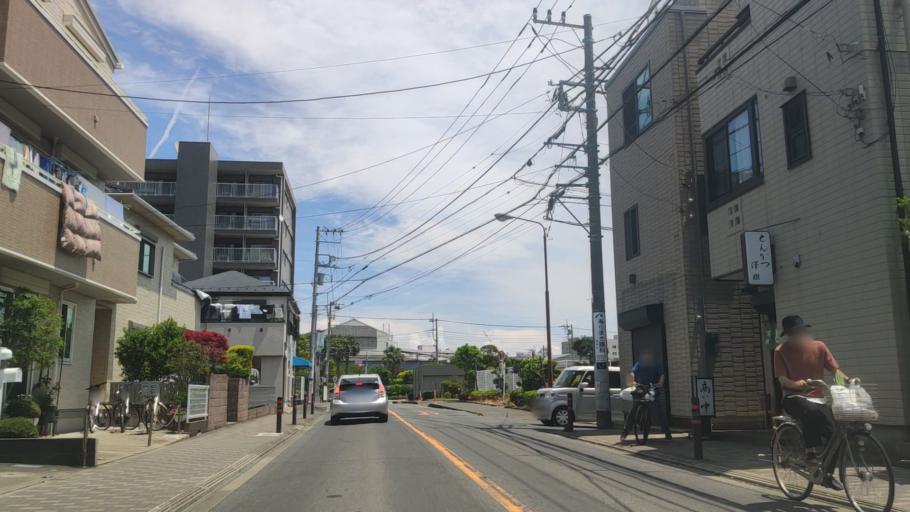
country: JP
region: Kanagawa
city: Chigasaki
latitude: 35.3367
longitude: 139.3973
